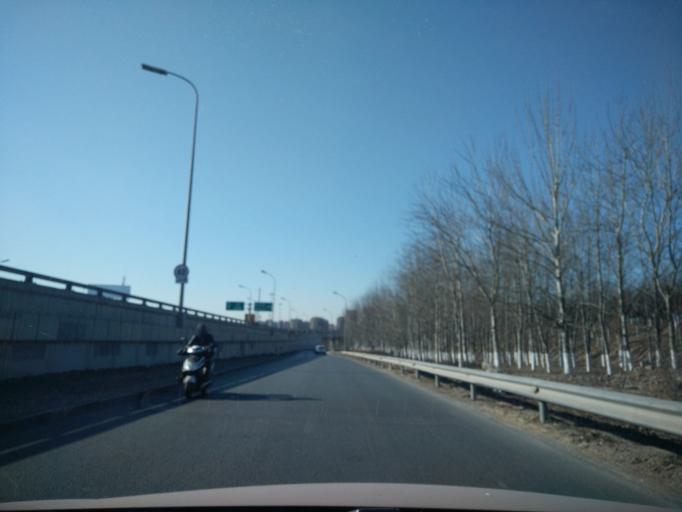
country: CN
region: Beijing
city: Jiugong
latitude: 39.7884
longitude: 116.4300
